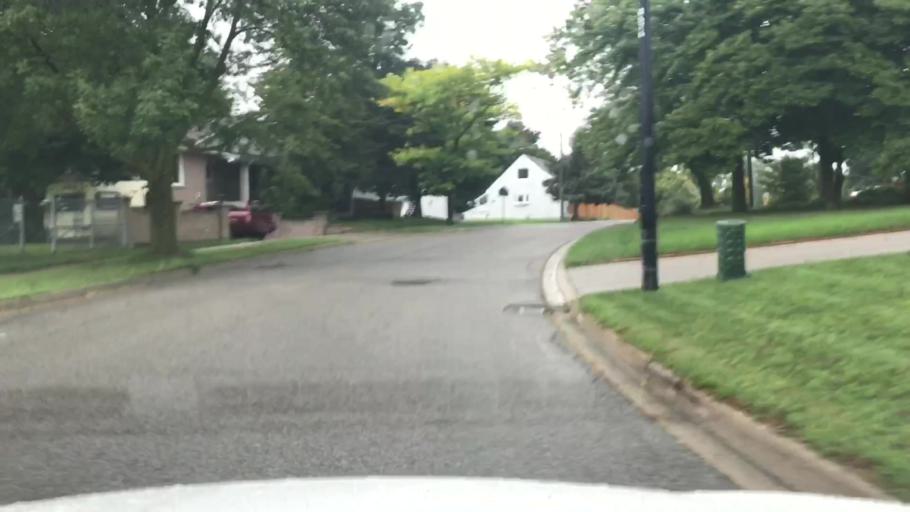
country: CA
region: Ontario
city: Newmarket
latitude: 44.0460
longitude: -79.4646
